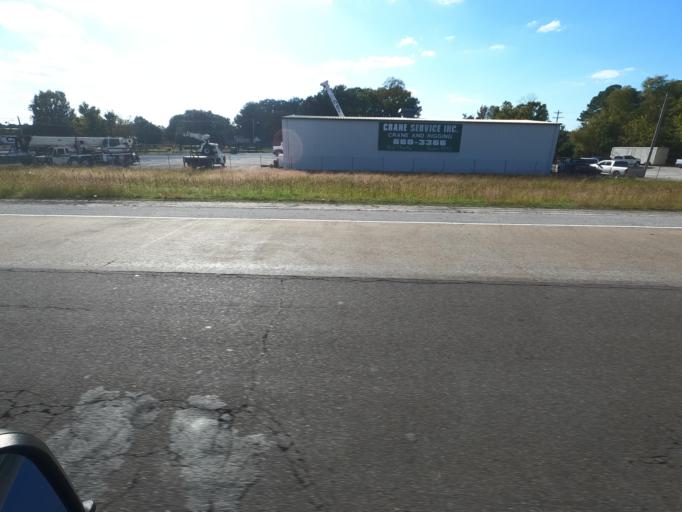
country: US
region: Tennessee
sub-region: Madison County
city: Jackson
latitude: 35.6616
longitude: -88.8795
